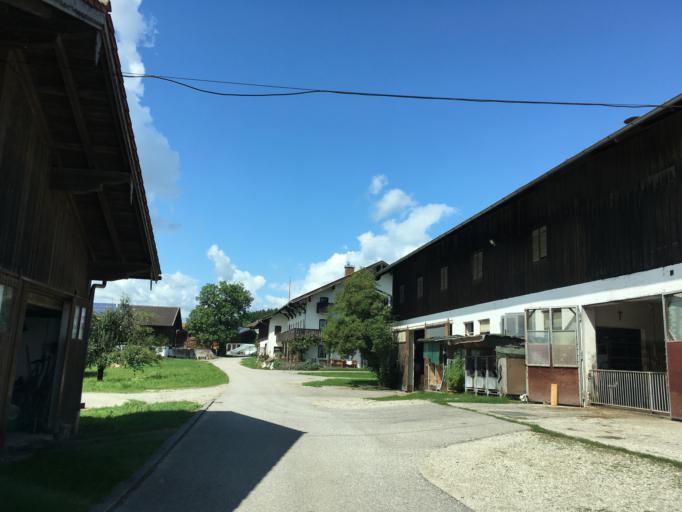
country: DE
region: Bavaria
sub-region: Upper Bavaria
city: Pittenhart
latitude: 47.9686
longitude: 12.3761
